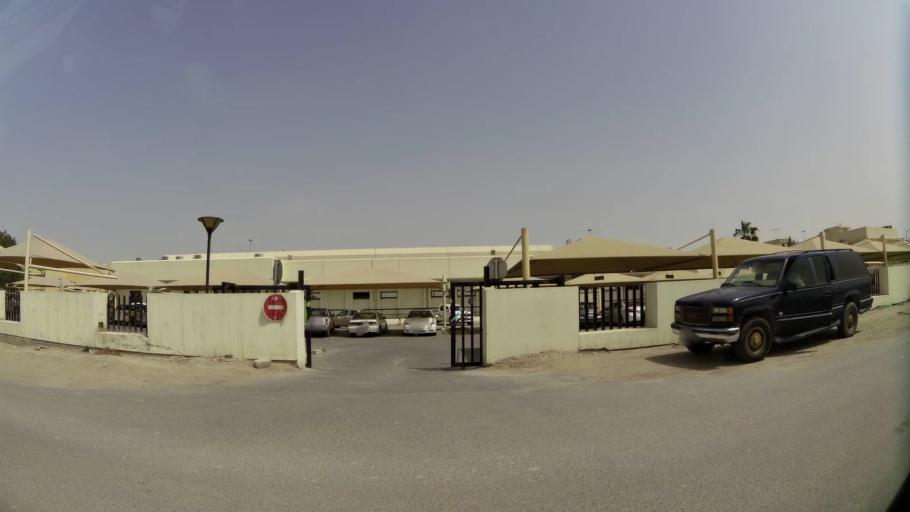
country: QA
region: Baladiyat ar Rayyan
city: Ar Rayyan
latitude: 25.2381
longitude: 51.4296
